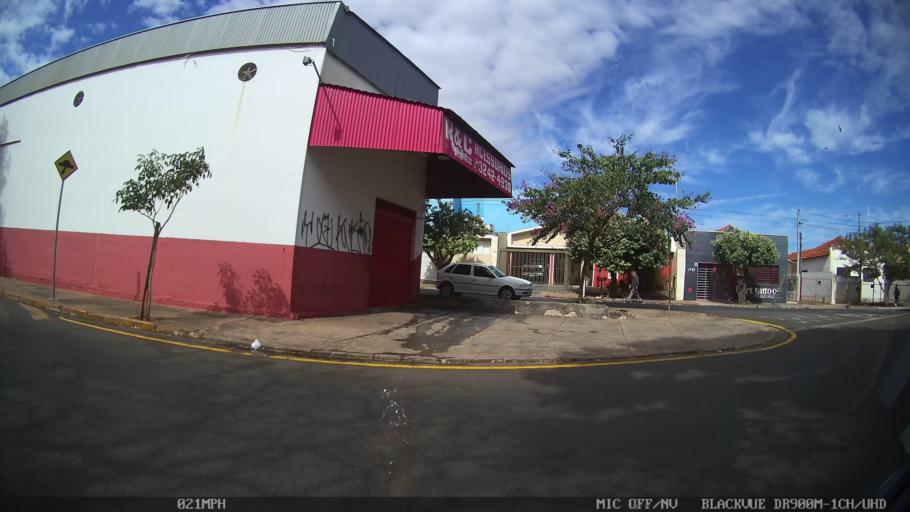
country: BR
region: Sao Paulo
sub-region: Bady Bassitt
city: Bady Bassitt
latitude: -20.8143
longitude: -49.5154
